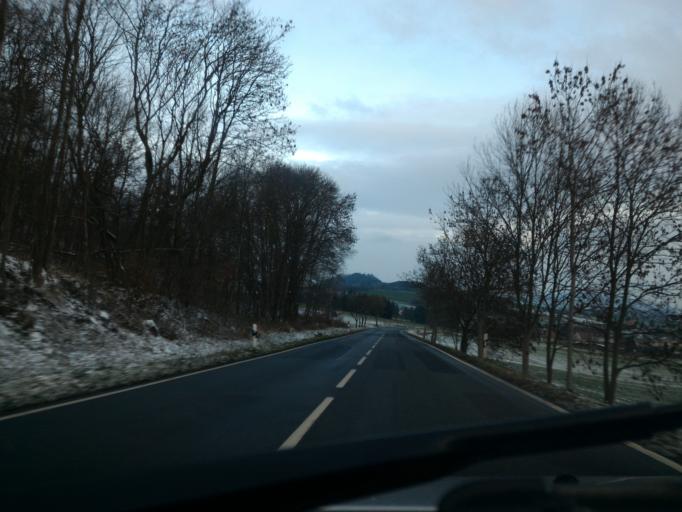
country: DE
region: Saxony
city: Leutersdorf
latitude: 50.9303
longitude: 14.6678
